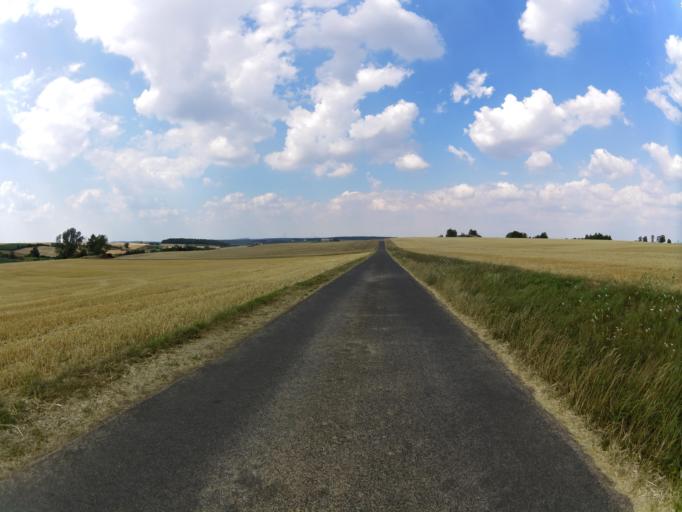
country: DE
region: Bavaria
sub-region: Regierungsbezirk Unterfranken
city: Ochsenfurt
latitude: 49.6460
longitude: 10.0650
